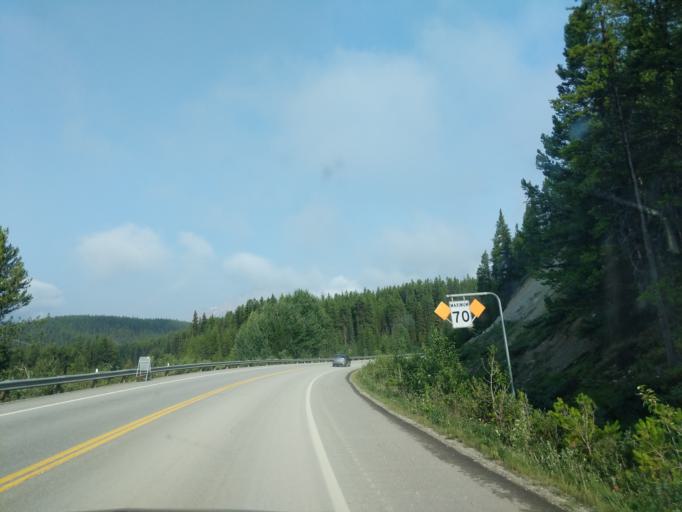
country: CA
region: Alberta
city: Lake Louise
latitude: 51.4449
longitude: -116.2117
